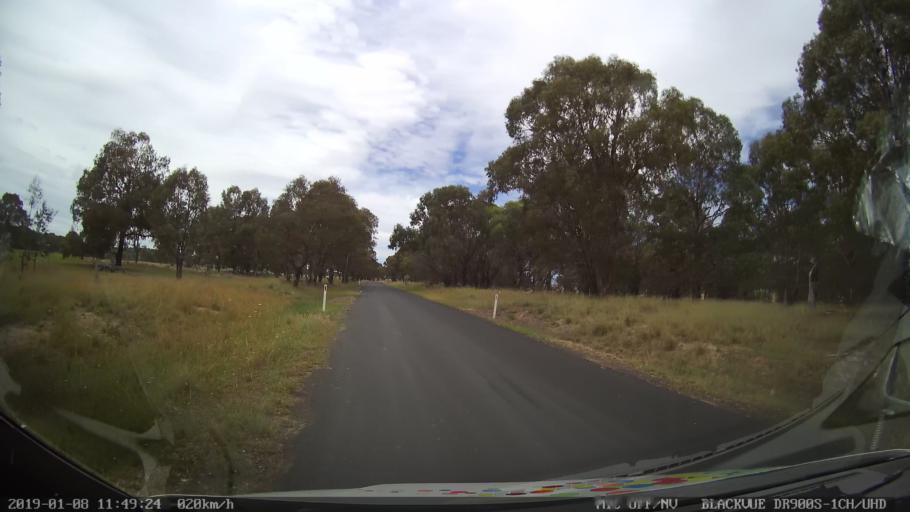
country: AU
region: New South Wales
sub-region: Armidale Dumaresq
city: Armidale
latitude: -30.3745
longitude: 151.5583
